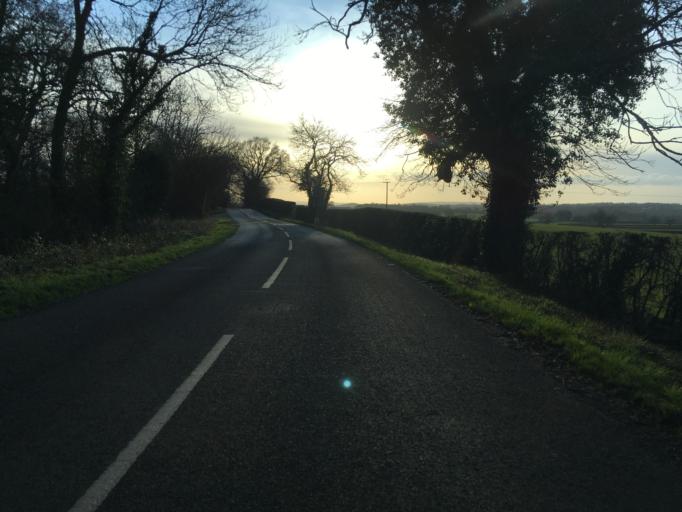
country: GB
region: England
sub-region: Warwickshire
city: Stratford-upon-Avon
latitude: 52.2256
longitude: -1.7334
